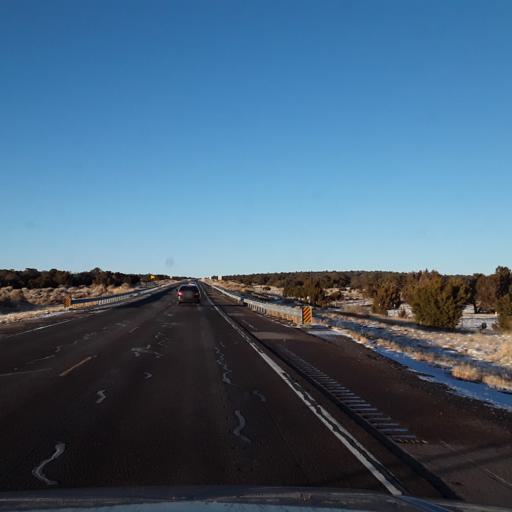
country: US
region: New Mexico
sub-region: Lincoln County
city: Carrizozo
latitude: 34.2055
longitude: -105.6485
